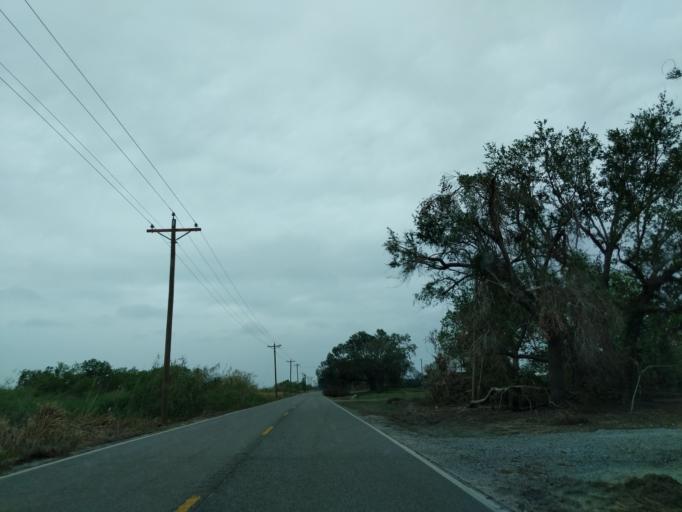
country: US
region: Louisiana
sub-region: Jefferson Davis Parish
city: Lake Arthur
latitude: 29.7531
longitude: -92.9135
